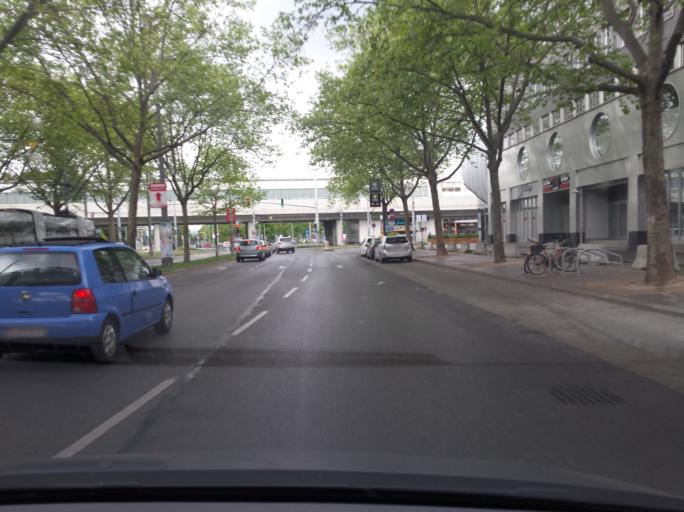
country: AT
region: Lower Austria
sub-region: Politischer Bezirk Wien-Umgebung
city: Gerasdorf bei Wien
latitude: 48.2425
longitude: 16.4342
